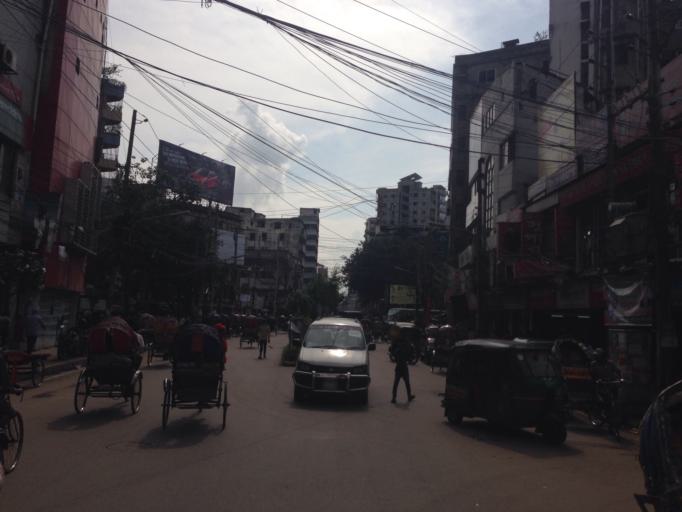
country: BD
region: Dhaka
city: Azimpur
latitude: 23.7397
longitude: 90.3891
